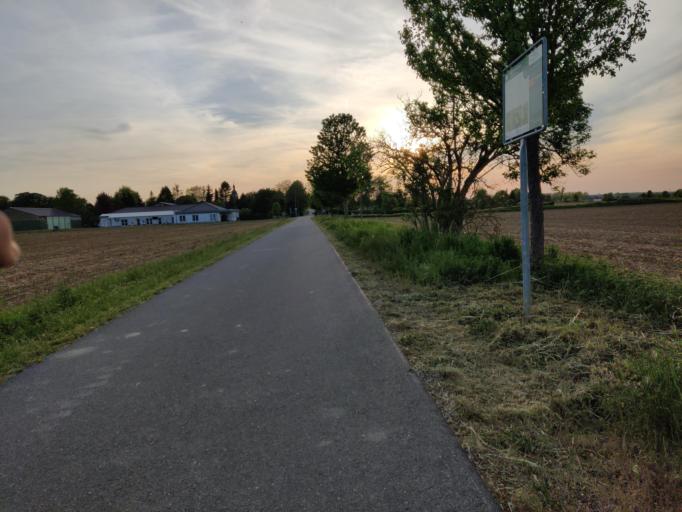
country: DE
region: Saxony-Anhalt
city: Laucha
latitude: 51.2232
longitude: 11.6908
